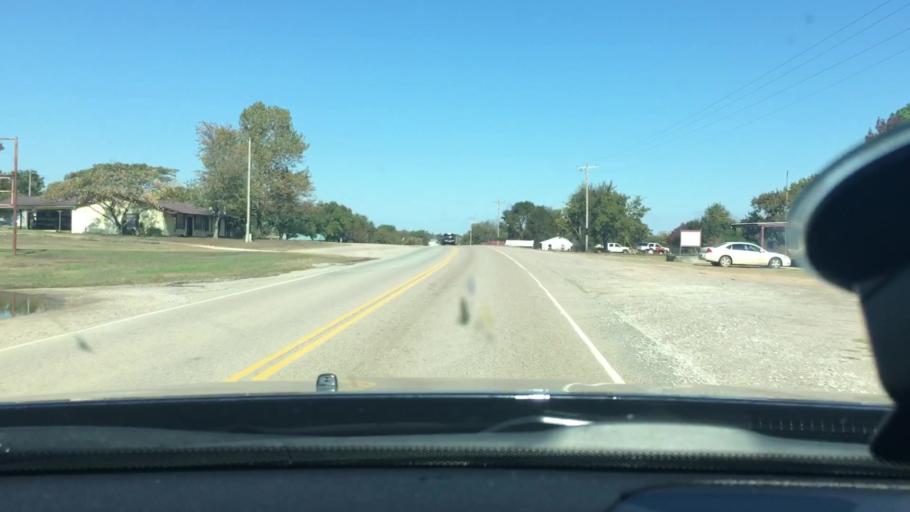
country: US
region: Oklahoma
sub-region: Johnston County
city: Tishomingo
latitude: 34.4422
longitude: -96.6359
